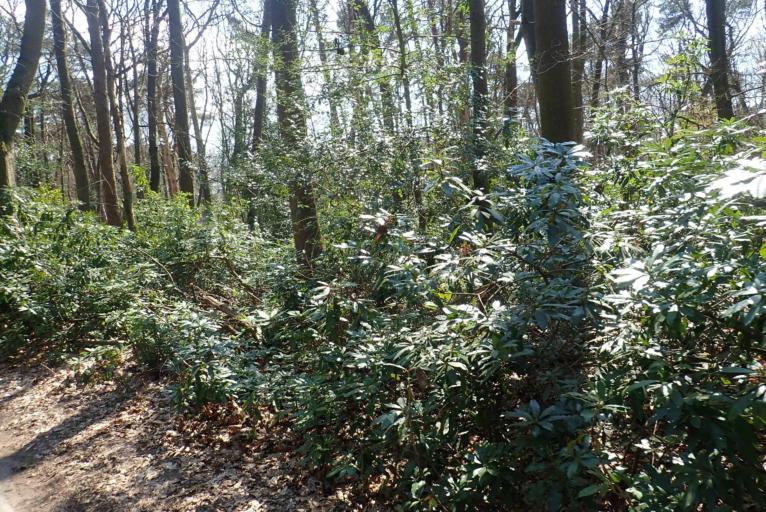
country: BE
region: Flanders
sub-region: Provincie Antwerpen
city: Kalmthout
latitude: 51.3505
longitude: 4.4698
